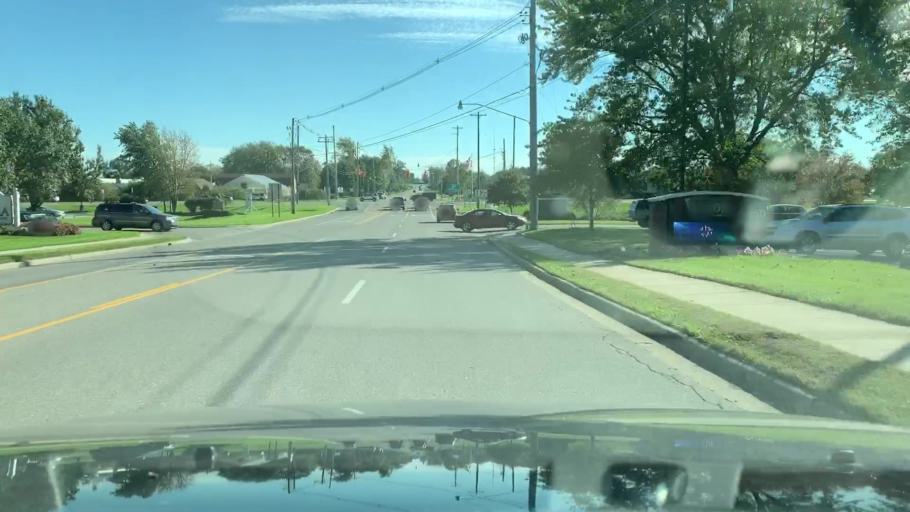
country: US
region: Michigan
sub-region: Ottawa County
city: Zeeland
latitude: 42.8068
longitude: -86.0189
